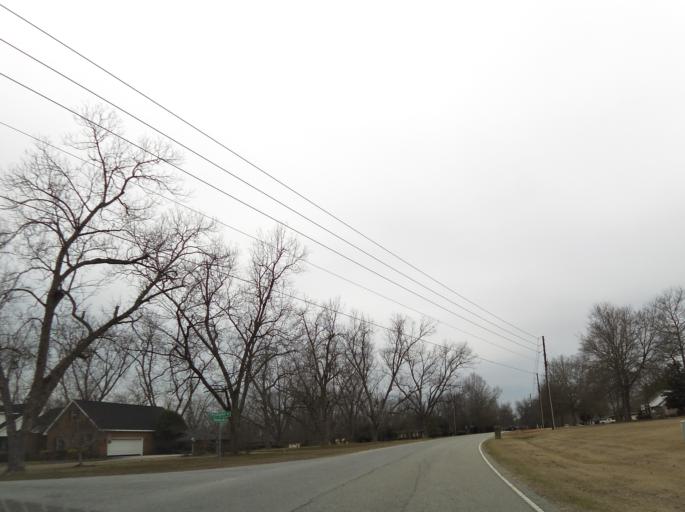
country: US
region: Georgia
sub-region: Houston County
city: Centerville
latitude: 32.7016
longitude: -83.6845
